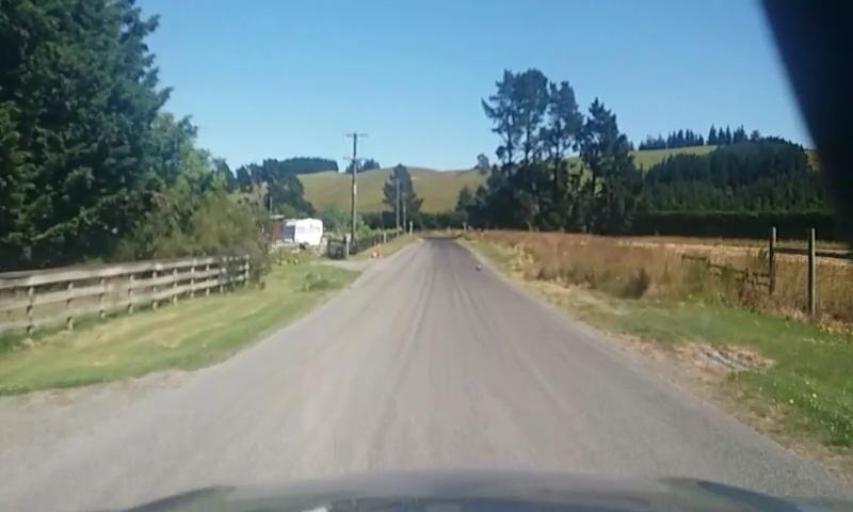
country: NZ
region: Canterbury
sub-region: Selwyn District
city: Darfield
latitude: -43.4797
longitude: 171.9602
